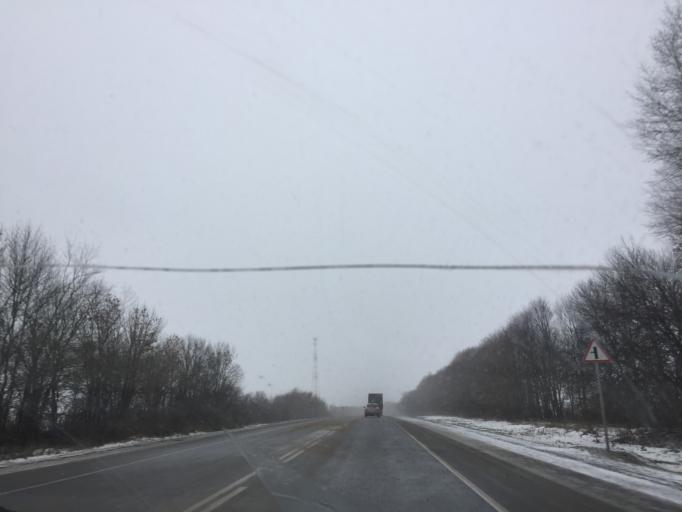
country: RU
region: Tula
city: Plavsk
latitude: 53.7882
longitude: 37.3667
